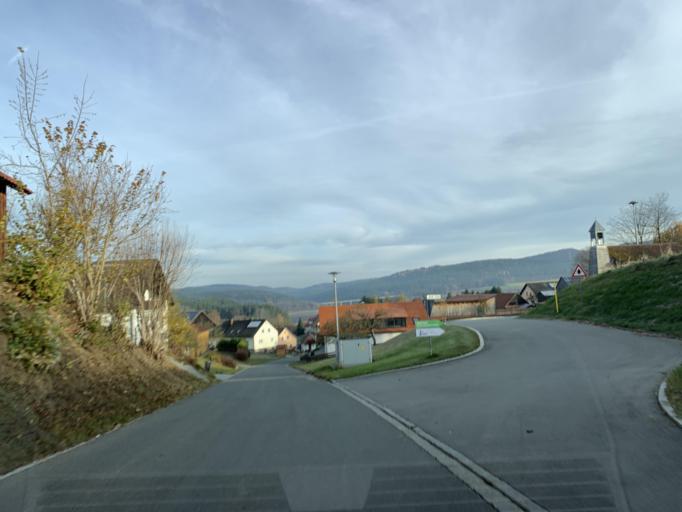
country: DE
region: Bavaria
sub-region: Upper Palatinate
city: Neukirchen-Balbini
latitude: 49.3336
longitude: 12.4395
